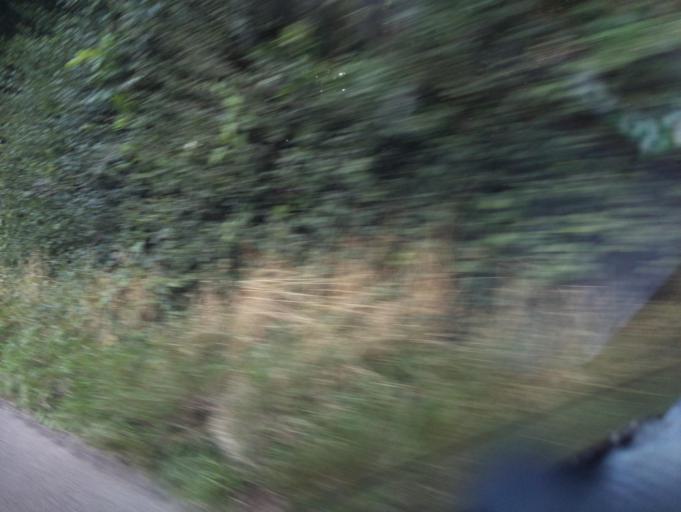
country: GB
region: England
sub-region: Devon
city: Tiverton
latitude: 50.8755
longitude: -3.4937
